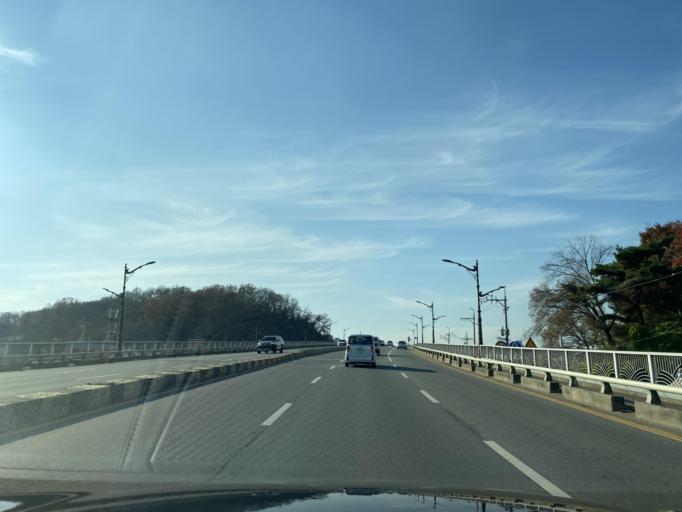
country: KR
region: Chungcheongnam-do
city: Cheonan
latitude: 36.7983
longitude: 127.1497
